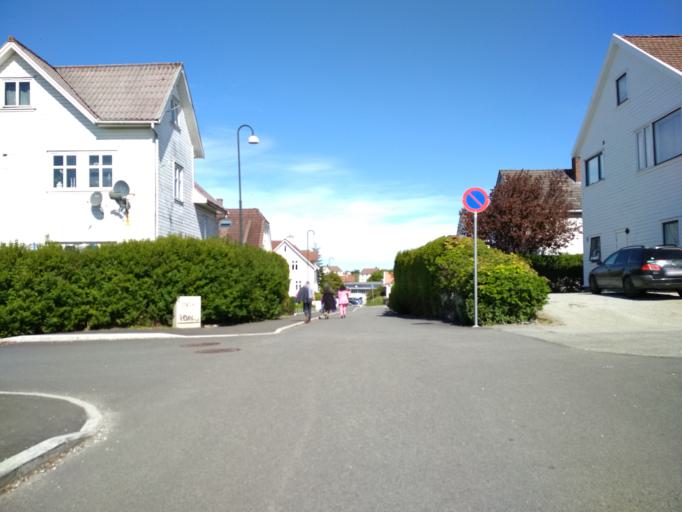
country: NO
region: Rogaland
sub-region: Stavanger
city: Stavanger
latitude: 58.9735
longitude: 5.7140
